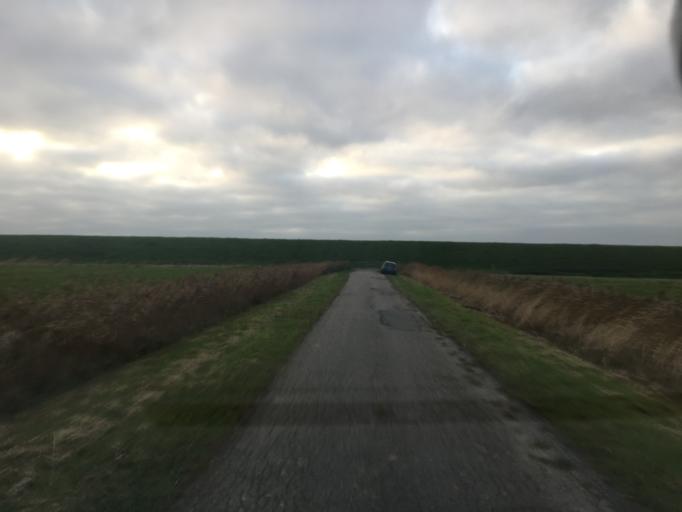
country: DE
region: Schleswig-Holstein
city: Klanxbull
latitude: 54.9274
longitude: 8.6704
